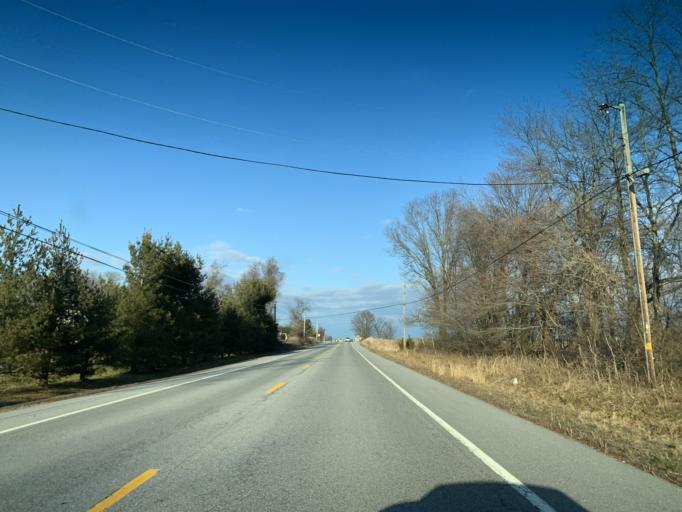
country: US
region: Maryland
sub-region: Queen Anne's County
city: Kingstown
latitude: 39.1708
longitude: -75.9228
